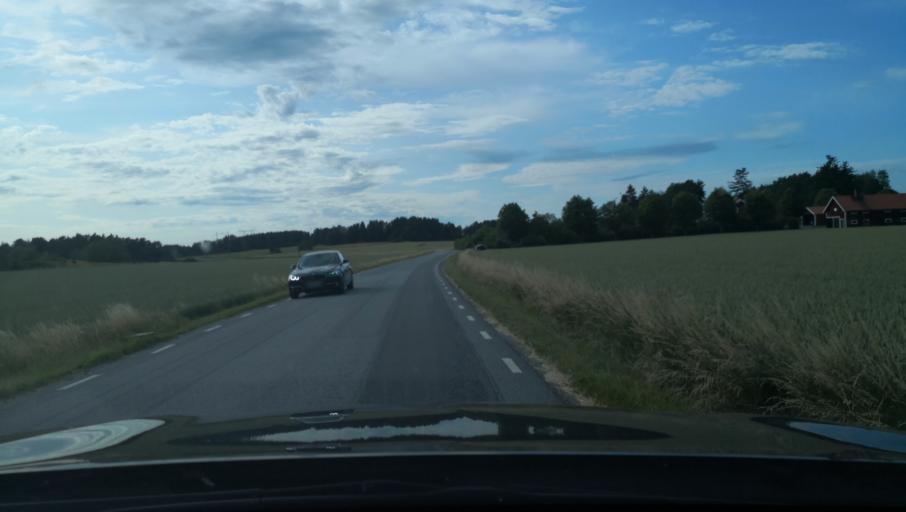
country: SE
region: Uppsala
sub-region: Habo Kommun
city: Balsta
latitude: 59.6719
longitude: 17.4371
